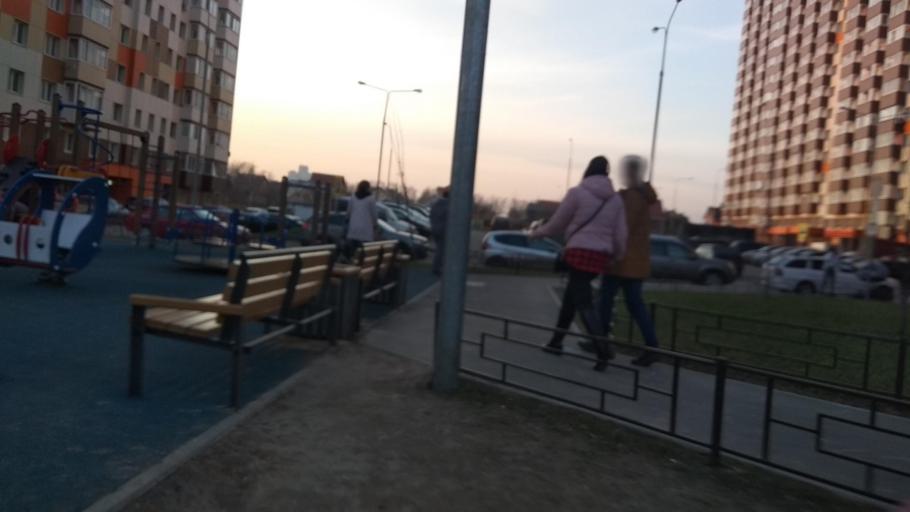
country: RU
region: Moskovskaya
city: Vidnoye
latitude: 55.5603
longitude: 37.7017
